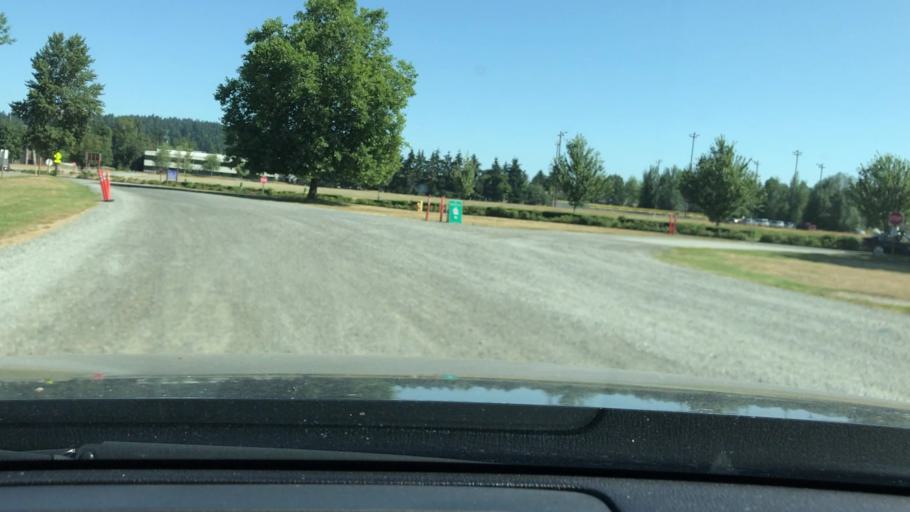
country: US
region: Washington
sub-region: King County
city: Redmond
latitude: 47.6608
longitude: -122.1108
